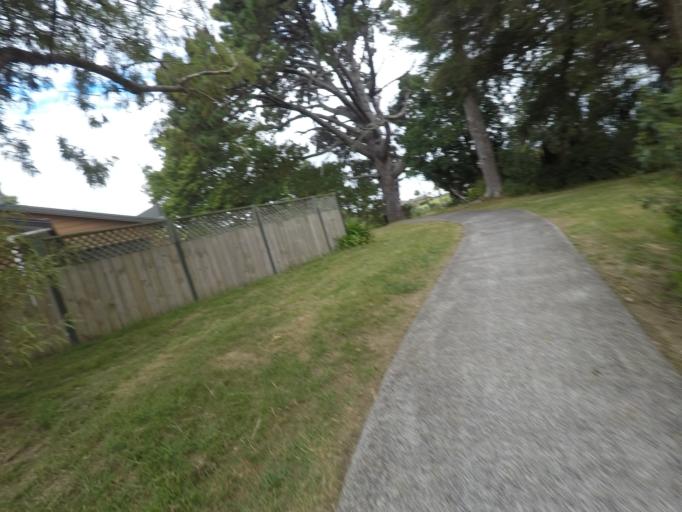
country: NZ
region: Auckland
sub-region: Auckland
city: Papakura
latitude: -37.0601
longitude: 174.9333
